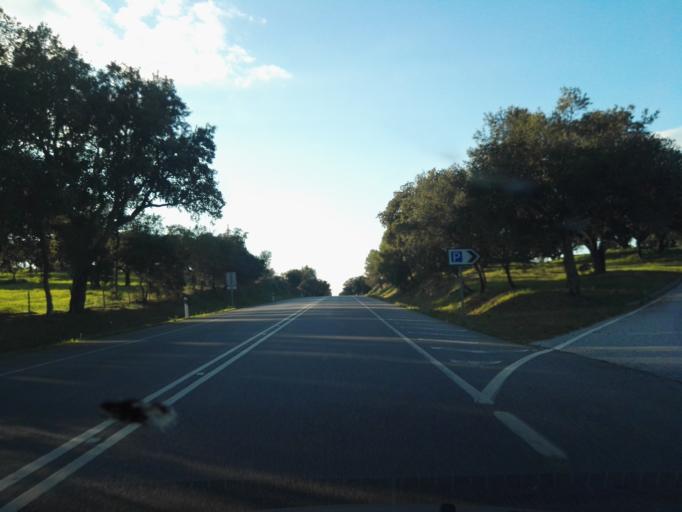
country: PT
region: Evora
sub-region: Montemor-O-Novo
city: Montemor-o-Novo
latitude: 38.6150
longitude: -8.0785
